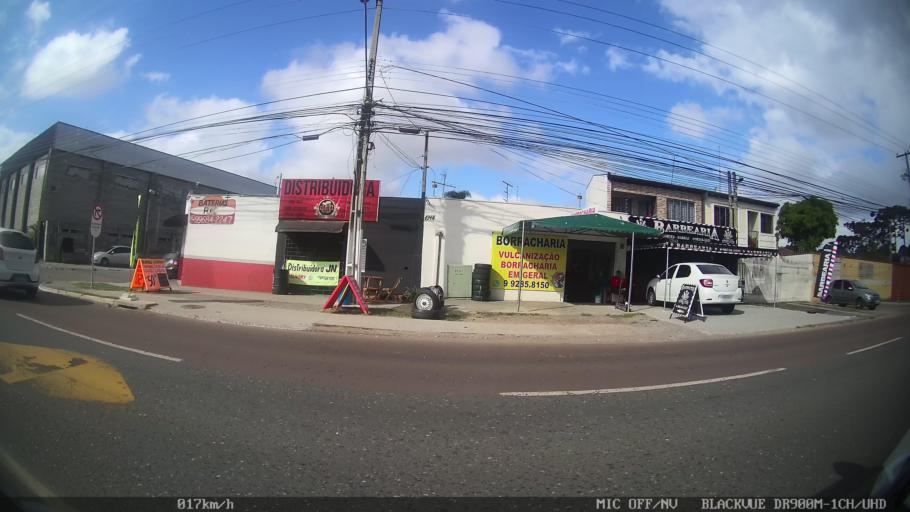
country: BR
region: Parana
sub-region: Pinhais
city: Pinhais
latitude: -25.4118
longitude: -49.1899
